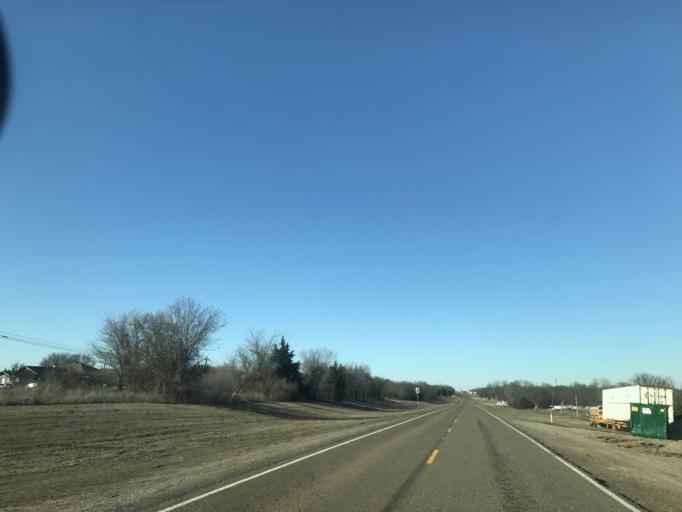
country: US
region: Texas
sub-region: Ellis County
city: Ferris
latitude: 32.5174
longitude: -96.6641
